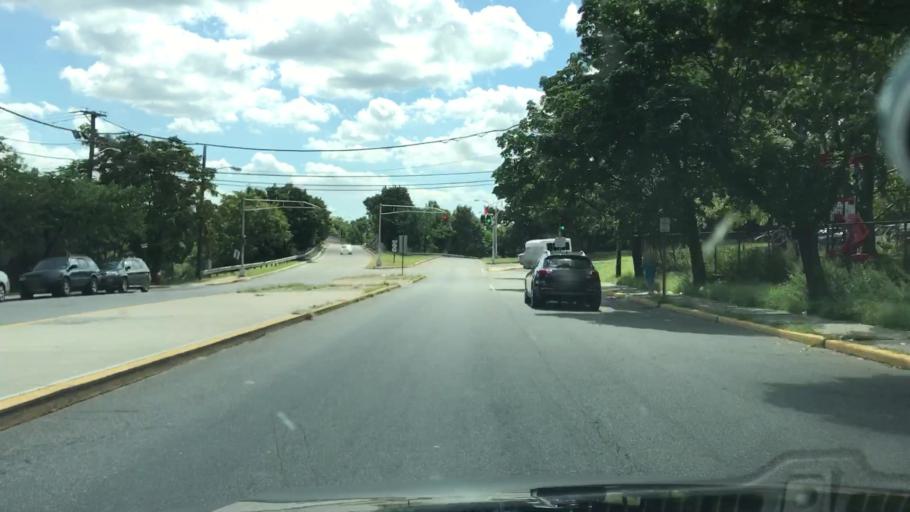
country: US
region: New Jersey
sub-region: Passaic County
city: Passaic
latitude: 40.8595
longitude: -74.1223
